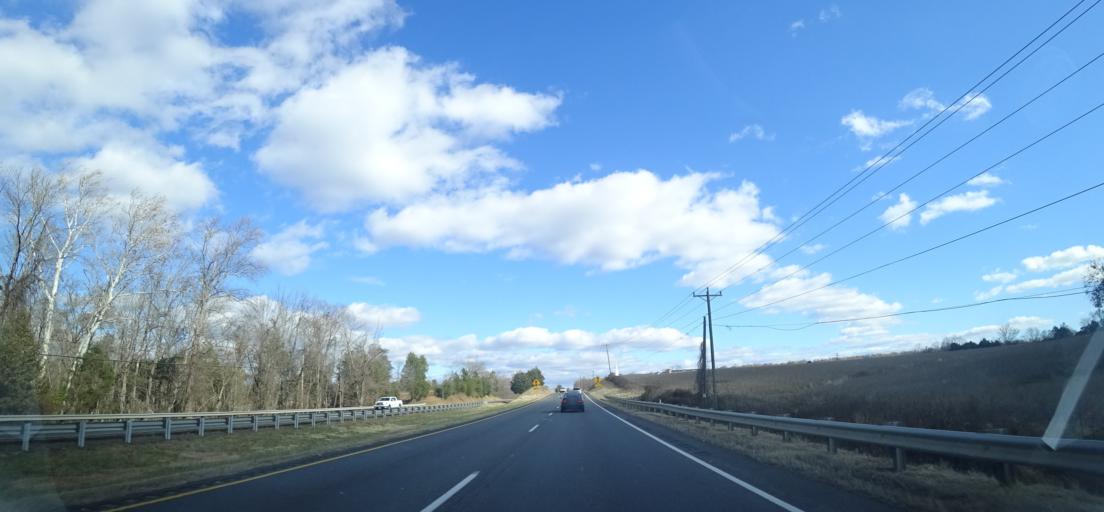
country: US
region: Virginia
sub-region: Fauquier County
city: New Baltimore
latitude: 38.7728
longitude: -77.6938
